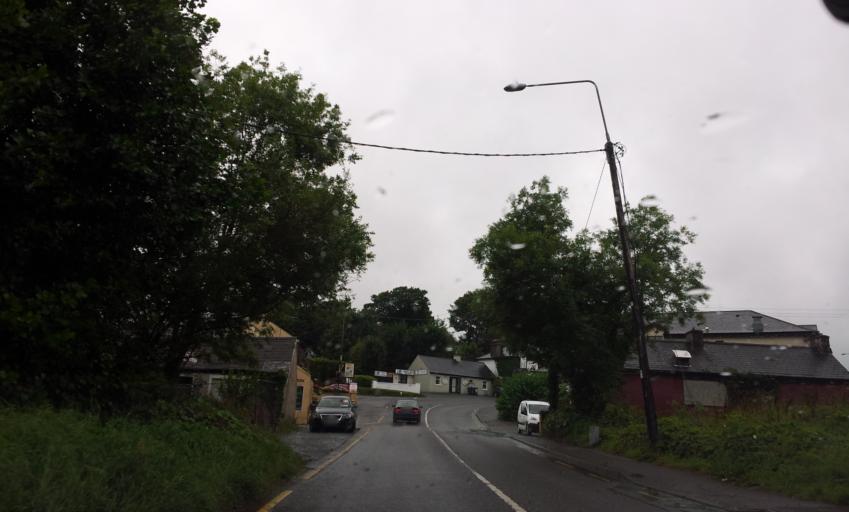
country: IE
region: Munster
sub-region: County Cork
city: Tower
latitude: 51.9255
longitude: -8.6067
